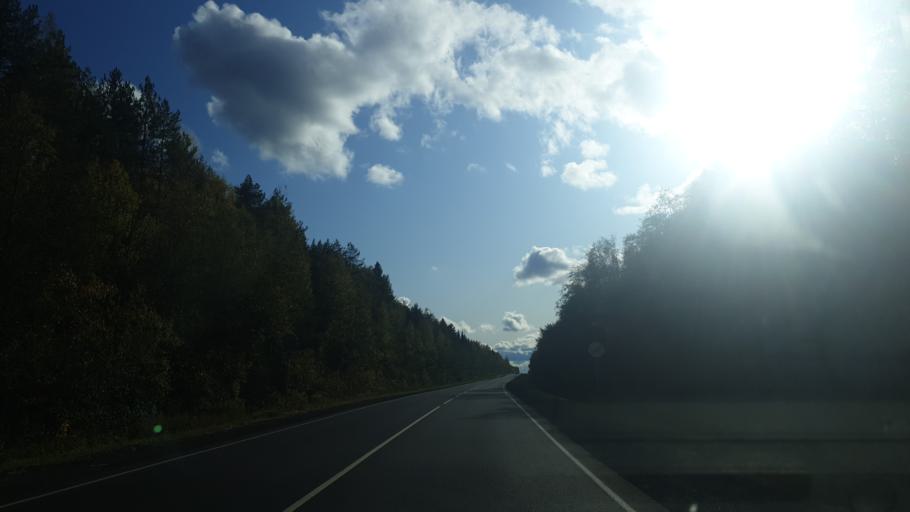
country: RU
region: Komi Republic
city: Letka
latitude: 60.3599
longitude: 49.6738
